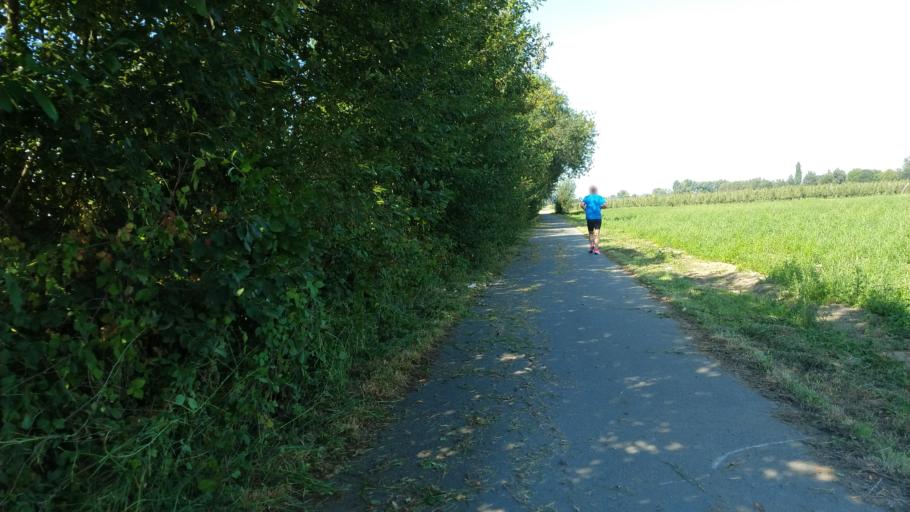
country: BE
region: Flanders
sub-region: Provincie Oost-Vlaanderen
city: Assenede
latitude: 51.2268
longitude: 3.7464
